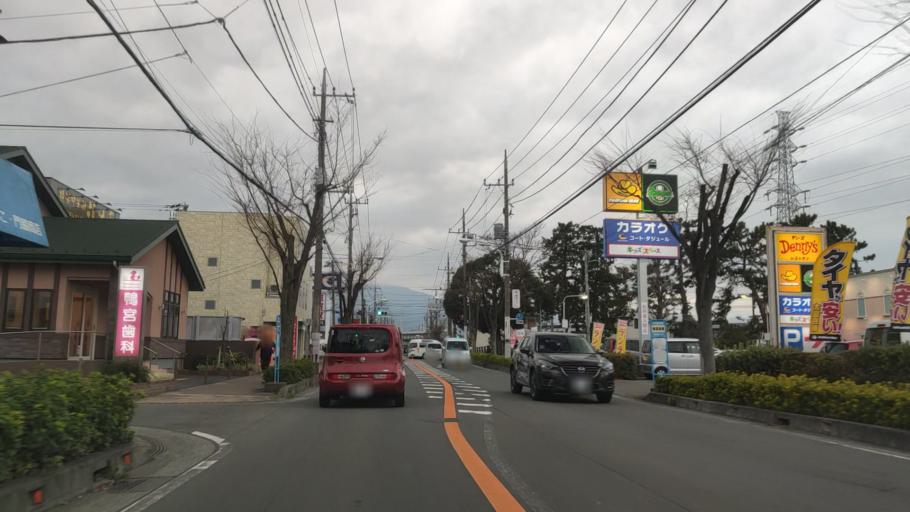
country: JP
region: Kanagawa
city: Odawara
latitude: 35.2799
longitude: 139.1842
